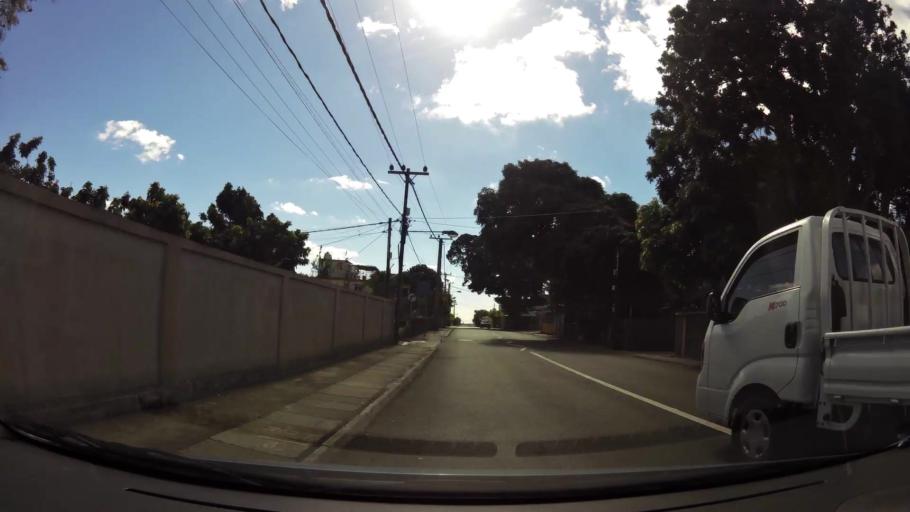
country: MU
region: Plaines Wilhems
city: Vacoas
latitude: -20.2814
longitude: 57.4787
